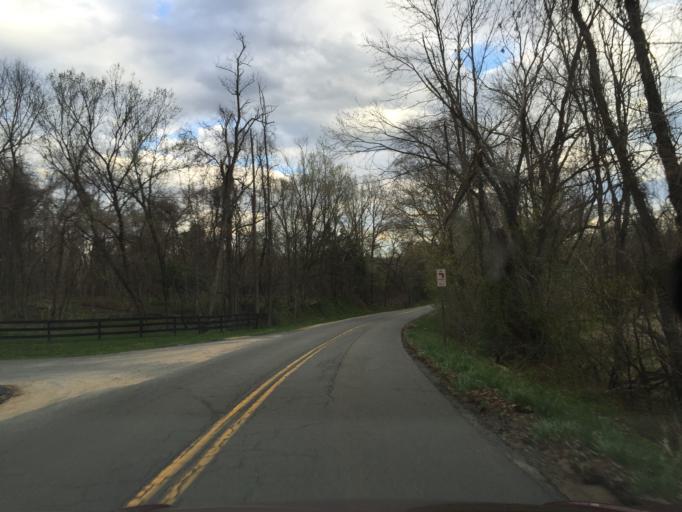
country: US
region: Maryland
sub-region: Frederick County
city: Point of Rocks
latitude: 39.2604
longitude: -77.5803
